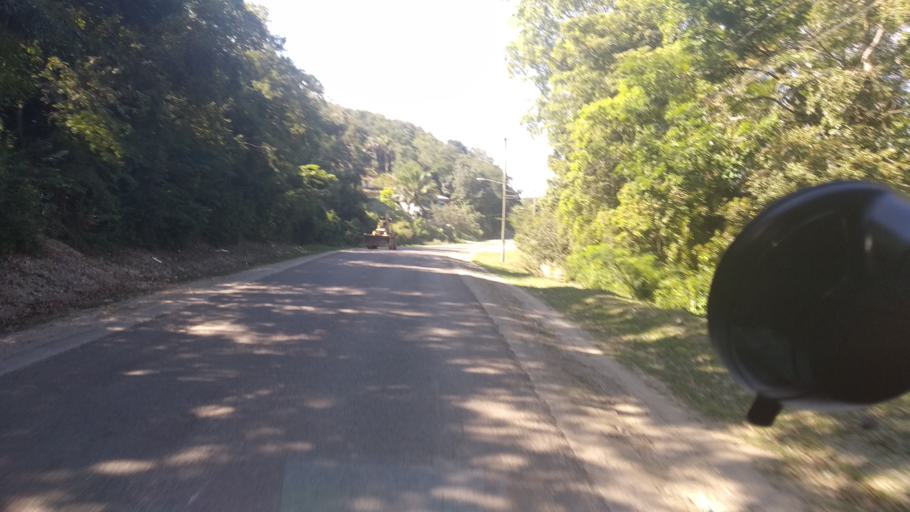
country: BZ
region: Cayo
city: Benque Viejo del Carmen
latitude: 17.0836
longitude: -89.1348
